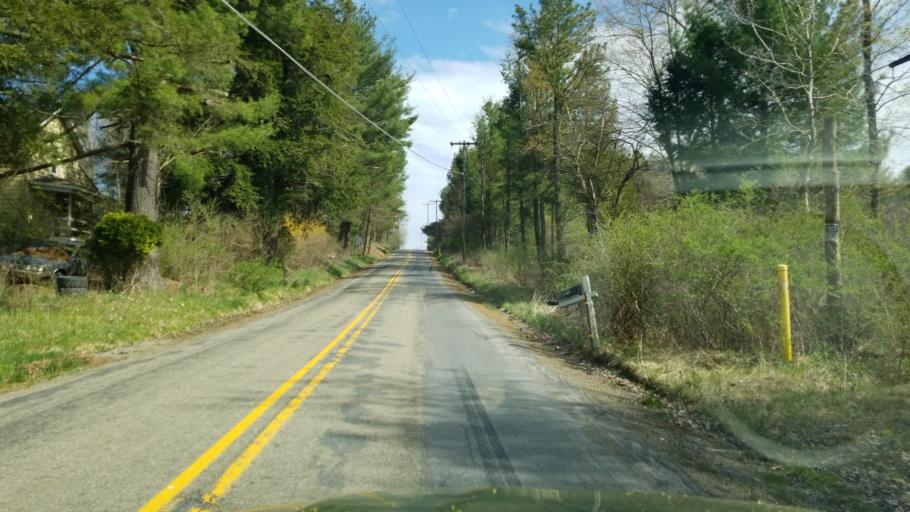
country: US
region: Pennsylvania
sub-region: Jefferson County
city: Brockway
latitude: 41.2246
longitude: -78.8517
